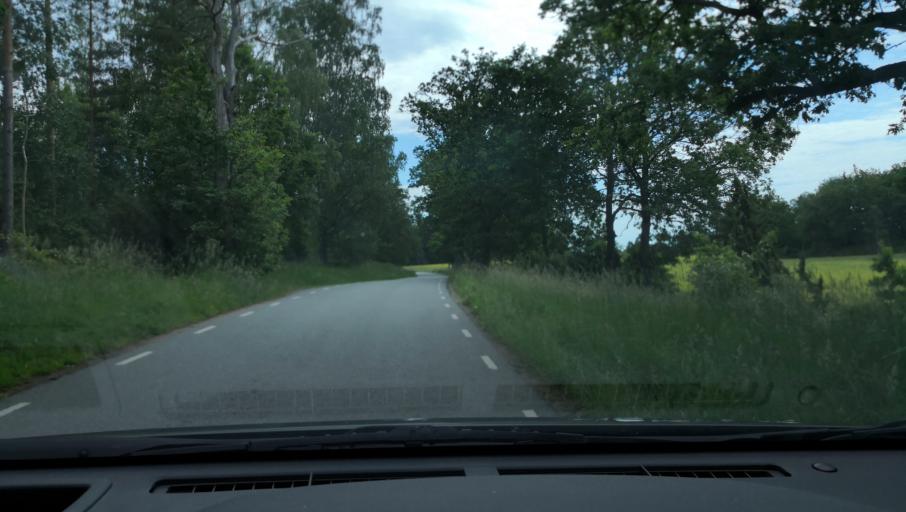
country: SE
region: Uppsala
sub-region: Enkopings Kommun
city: Orsundsbro
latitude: 59.7015
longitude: 17.4271
